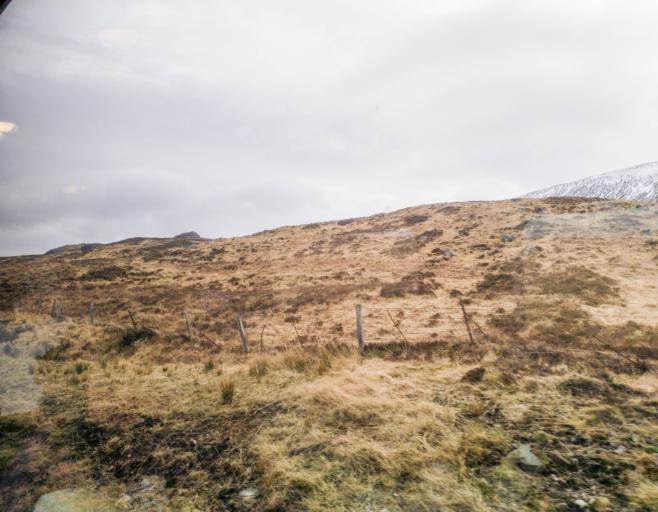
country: GB
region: Scotland
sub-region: Highland
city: Spean Bridge
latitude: 56.5861
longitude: -4.6627
